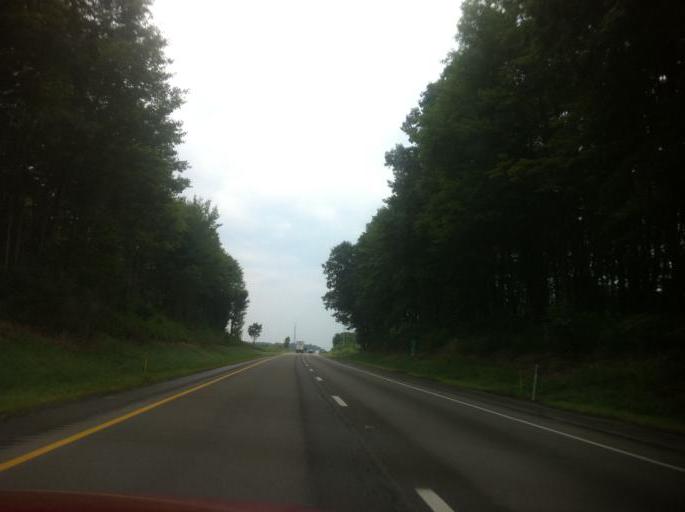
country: US
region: Pennsylvania
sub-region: Jefferson County
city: Brookville
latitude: 41.1807
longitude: -79.1392
